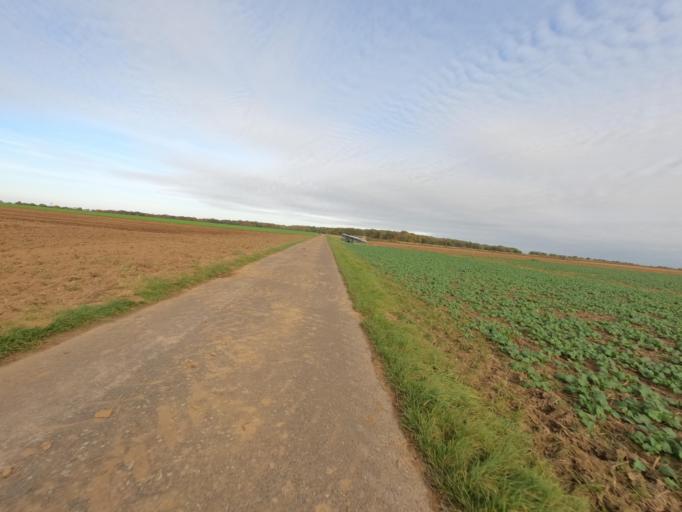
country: DE
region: North Rhine-Westphalia
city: Erkelenz
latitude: 51.0426
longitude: 6.3296
